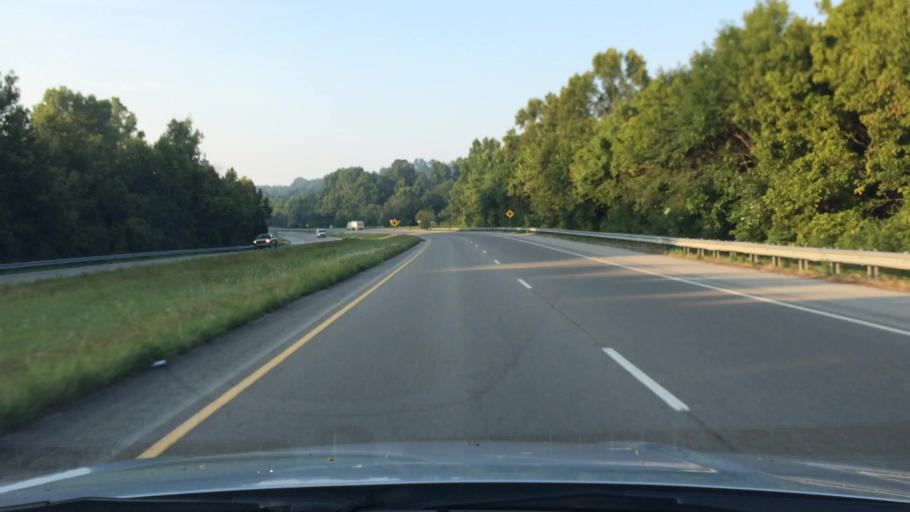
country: US
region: Tennessee
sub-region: Giles County
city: Pulaski
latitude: 35.1911
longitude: -87.0647
